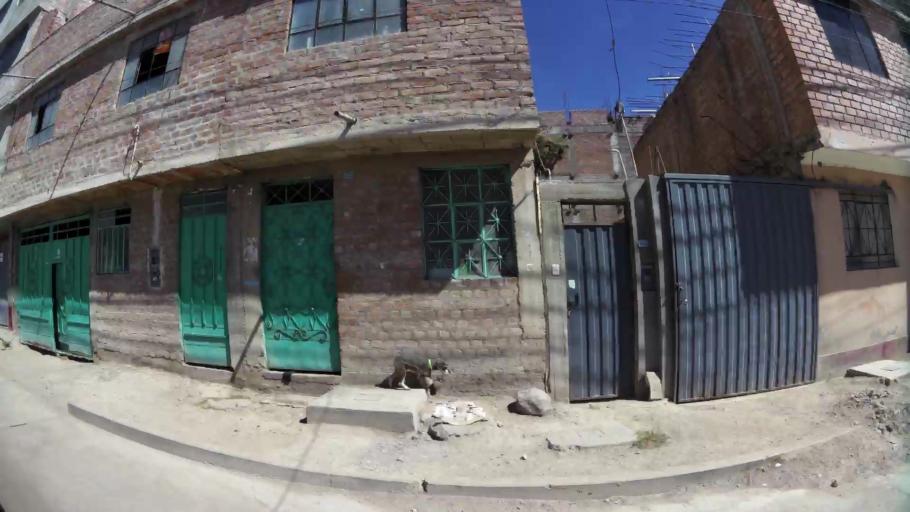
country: PE
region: Ayacucho
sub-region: Provincia de Huamanga
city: Ayacucho
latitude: -13.1549
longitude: -74.2328
